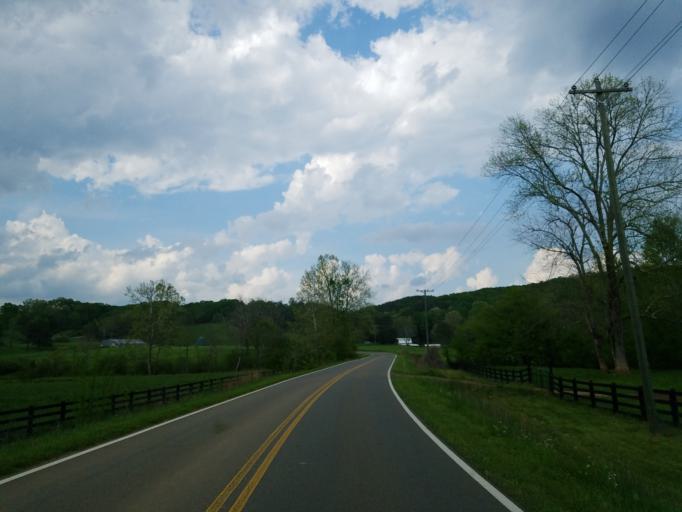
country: US
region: Georgia
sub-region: Pickens County
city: Jasper
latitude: 34.4330
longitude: -84.4522
